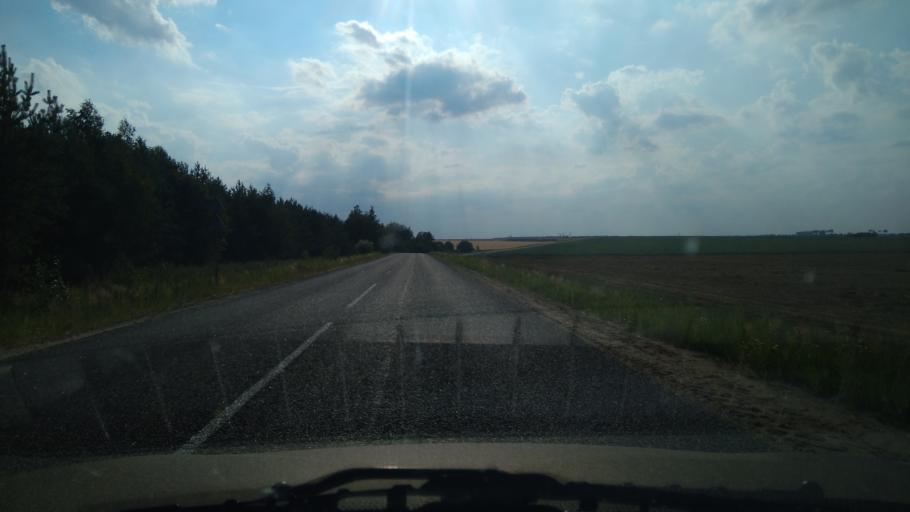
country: BY
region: Brest
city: Lyakhavichy
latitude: 53.0302
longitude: 26.3225
